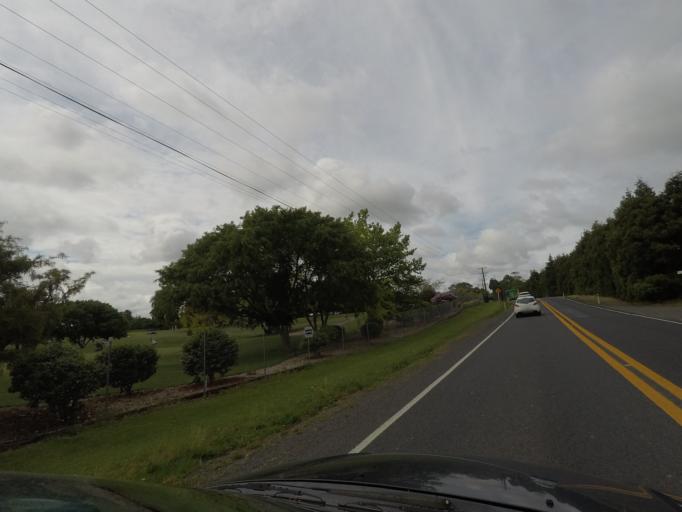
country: NZ
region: Auckland
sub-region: Auckland
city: Rosebank
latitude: -36.7730
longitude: 174.5873
